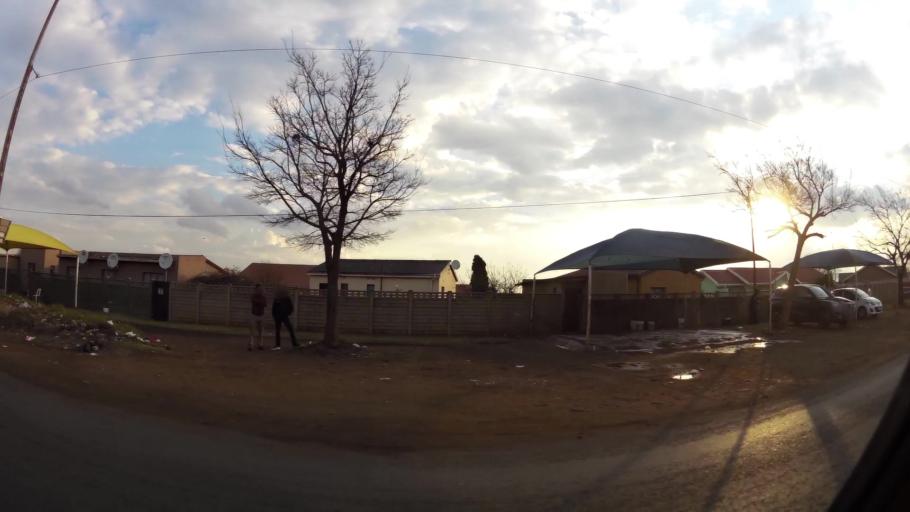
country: ZA
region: Gauteng
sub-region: City of Johannesburg Metropolitan Municipality
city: Orange Farm
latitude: -26.5890
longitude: 27.8466
